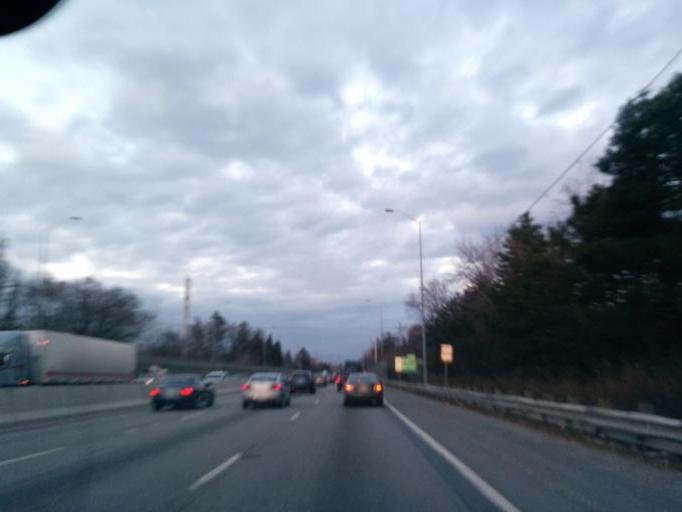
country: CA
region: Ontario
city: Mississauga
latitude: 43.5575
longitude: -79.6092
